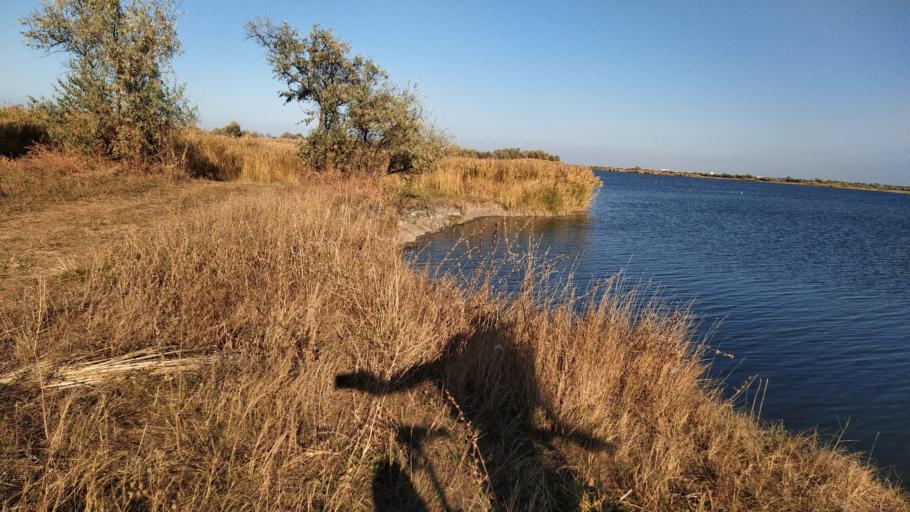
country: RU
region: Rostov
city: Kuleshovka
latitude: 47.1217
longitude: 39.6182
